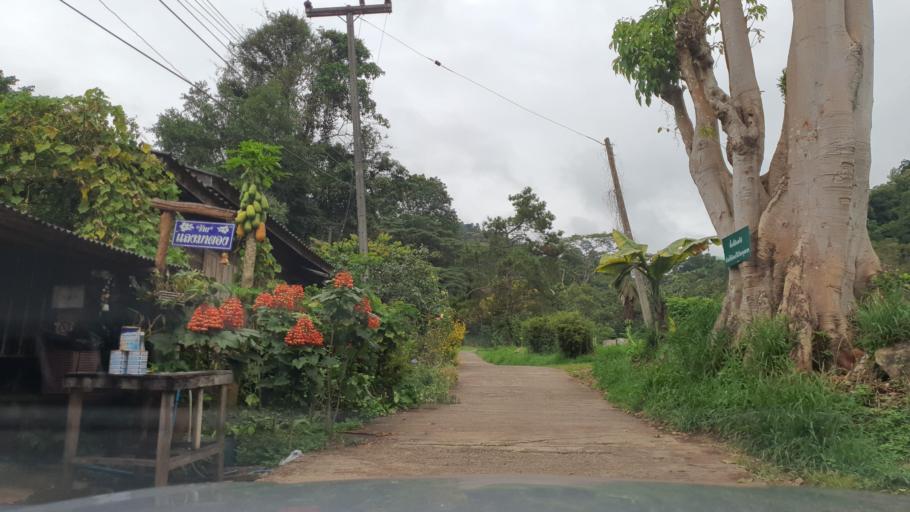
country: TH
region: Chiang Mai
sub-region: Amphoe Chiang Dao
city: Chiang Dao
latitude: 19.2514
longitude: 98.9225
